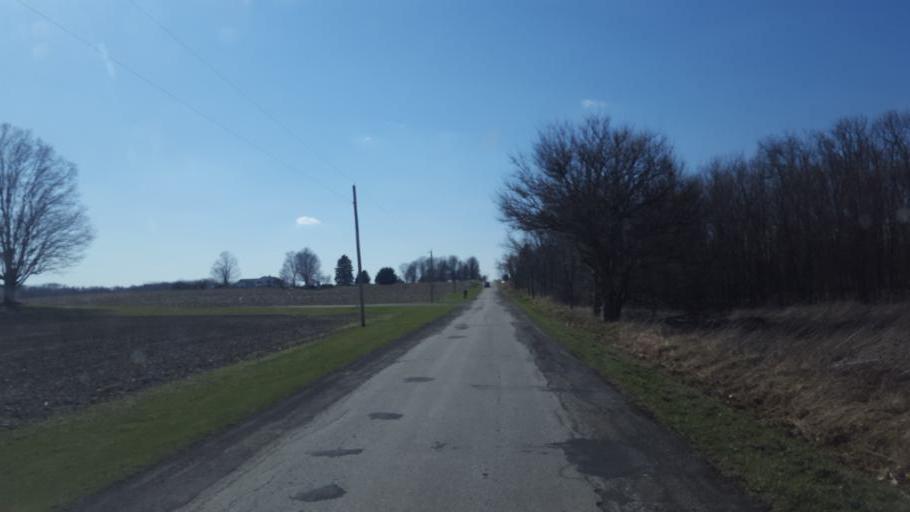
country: US
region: Ohio
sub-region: Morrow County
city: Mount Gilead
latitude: 40.4971
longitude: -82.7542
